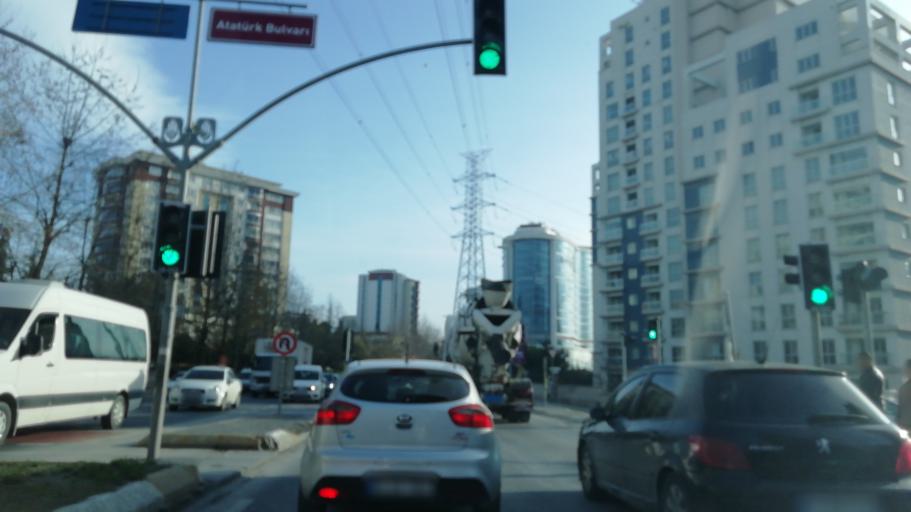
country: TR
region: Istanbul
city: Esenyurt
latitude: 41.0591
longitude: 28.6706
